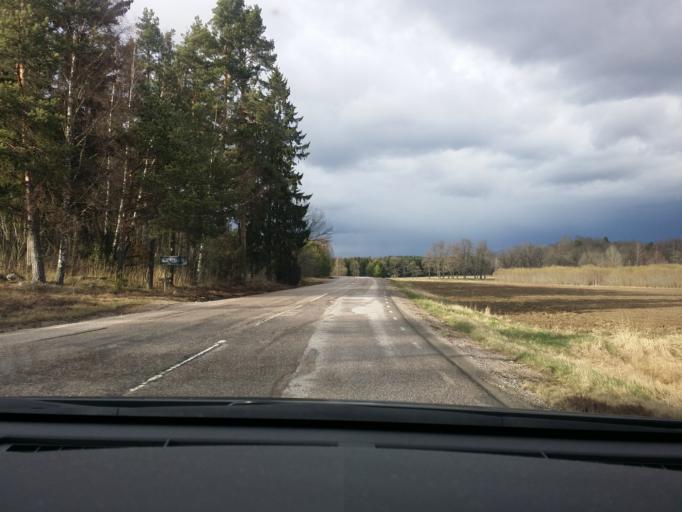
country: SE
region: Soedermanland
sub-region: Eskilstuna Kommun
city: Arla
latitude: 59.3043
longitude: 16.6819
